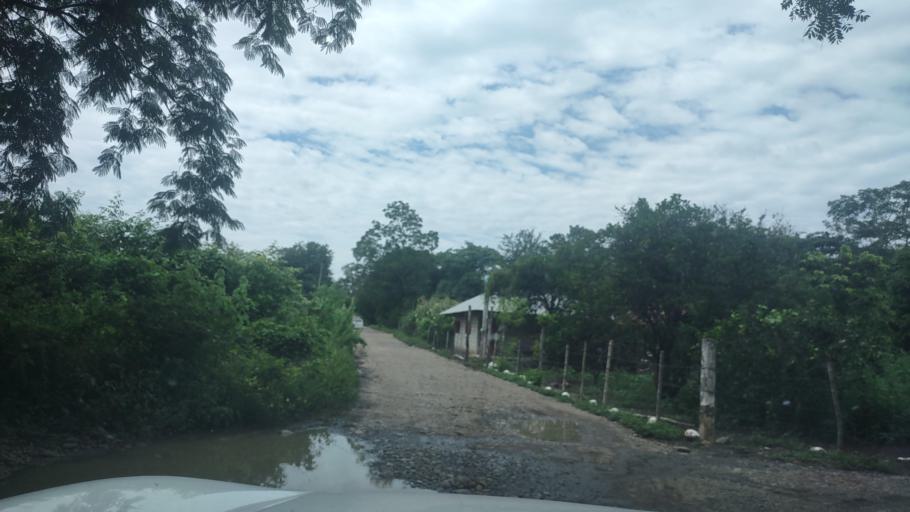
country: MX
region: Veracruz
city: Tepetzintla
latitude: 21.0465
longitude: -97.9994
